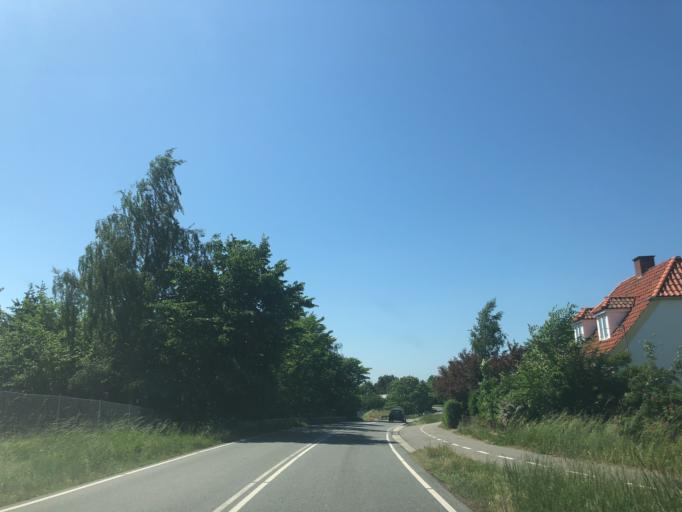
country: DK
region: Capital Region
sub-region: Gribskov Kommune
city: Graested
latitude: 56.0554
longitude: 12.2666
